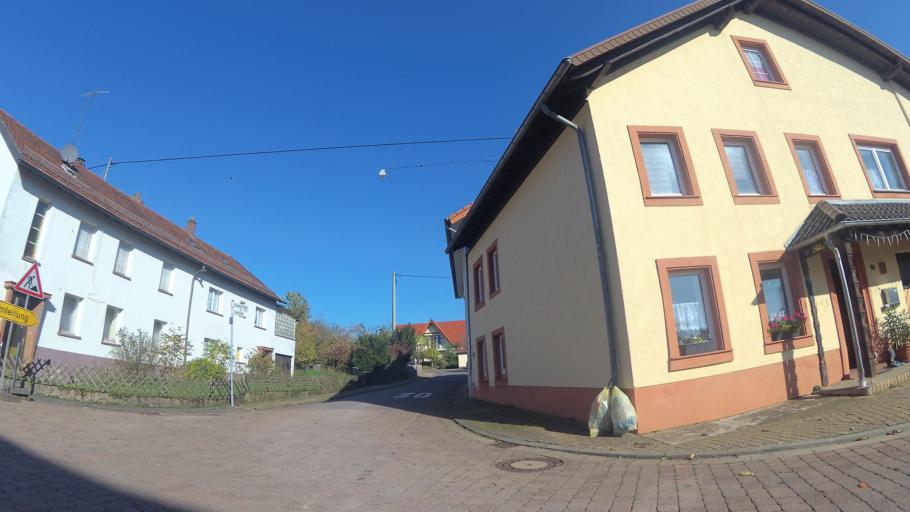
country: DE
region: Saarland
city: Britten
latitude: 49.5329
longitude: 6.6960
